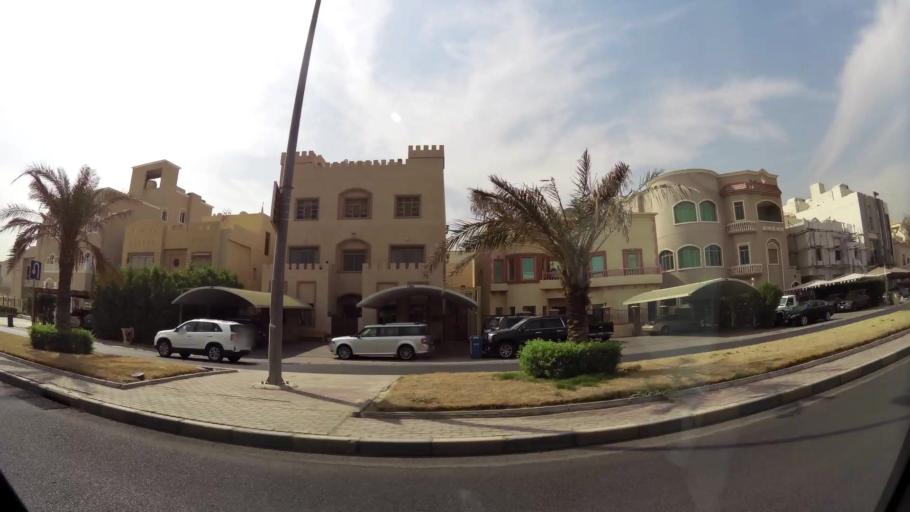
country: KW
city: Bayan
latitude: 29.2968
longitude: 48.0148
